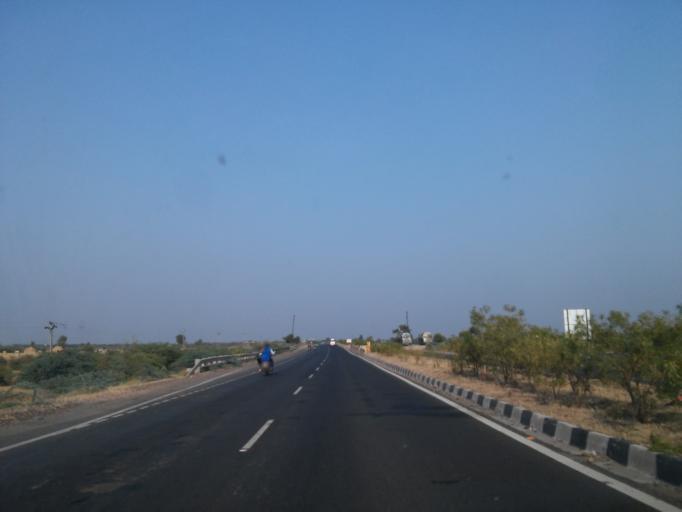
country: IN
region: Gujarat
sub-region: Surendranagar
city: Lakhtar
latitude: 23.0550
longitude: 71.7194
